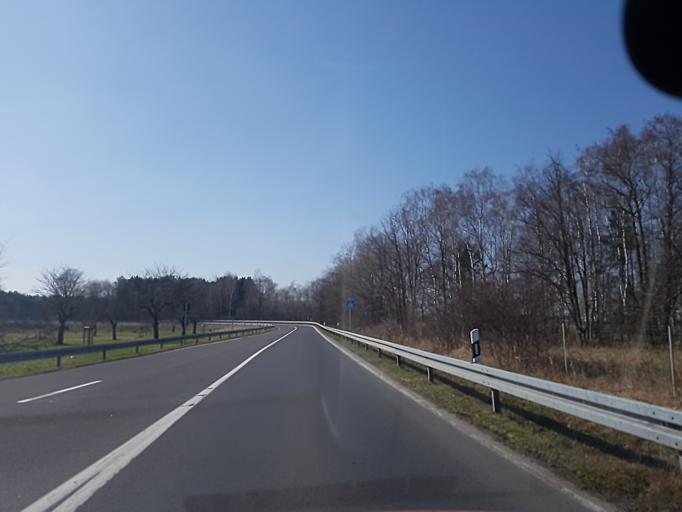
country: DE
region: Brandenburg
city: Forst
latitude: 51.7129
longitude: 14.6117
